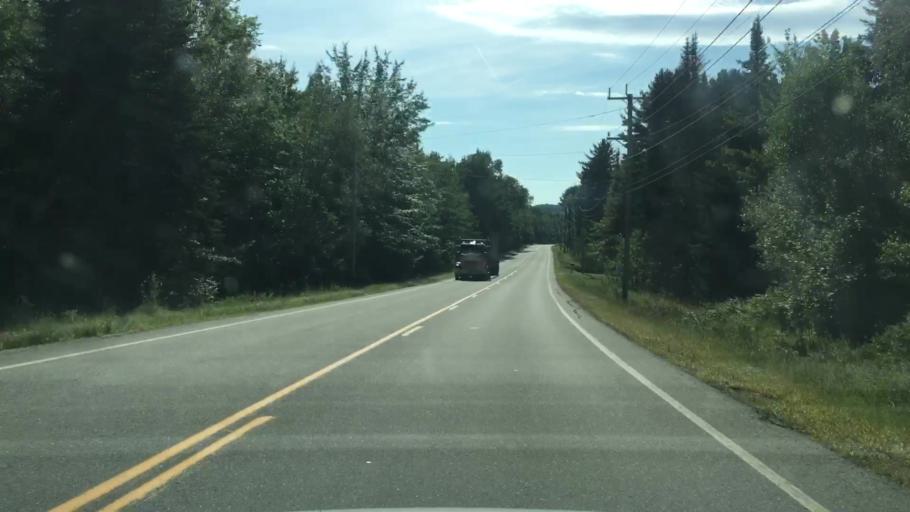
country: US
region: Maine
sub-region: Penobscot County
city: Lincoln
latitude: 45.3956
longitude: -68.5131
